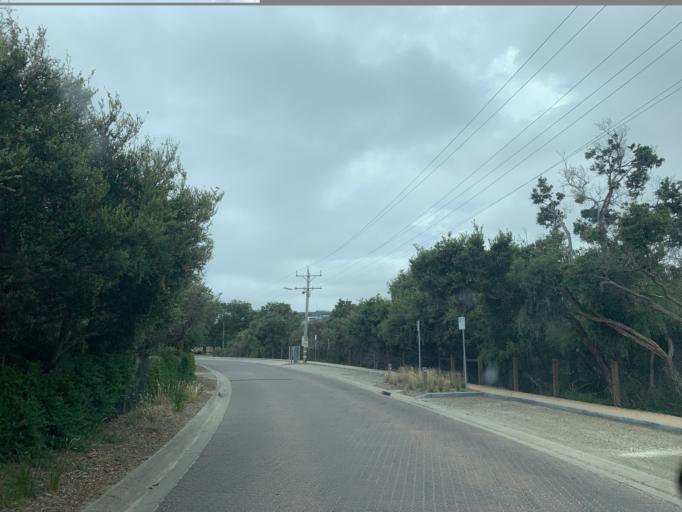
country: AU
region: Victoria
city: Hampton
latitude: -37.9467
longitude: 144.9995
